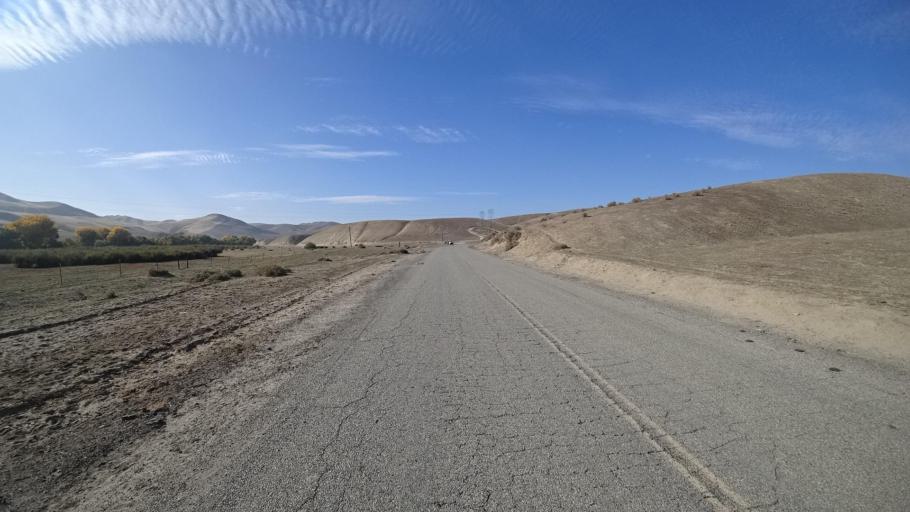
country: US
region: California
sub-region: Kern County
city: Oildale
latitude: 35.5181
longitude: -118.9162
